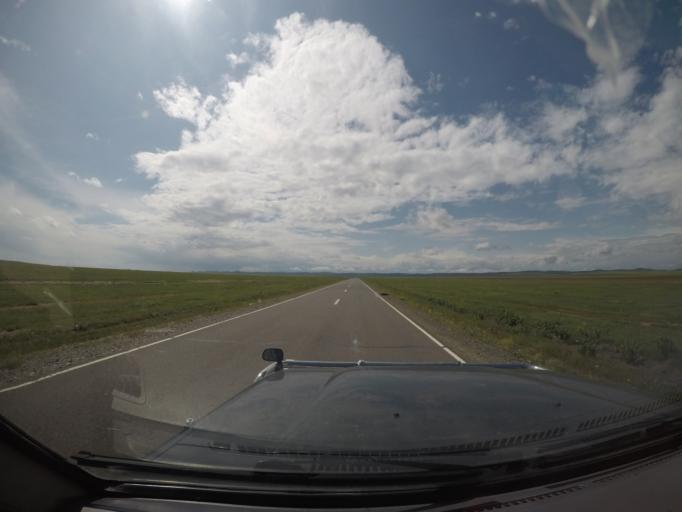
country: MN
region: Hentiy
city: Moron
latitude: 47.4195
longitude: 109.9888
